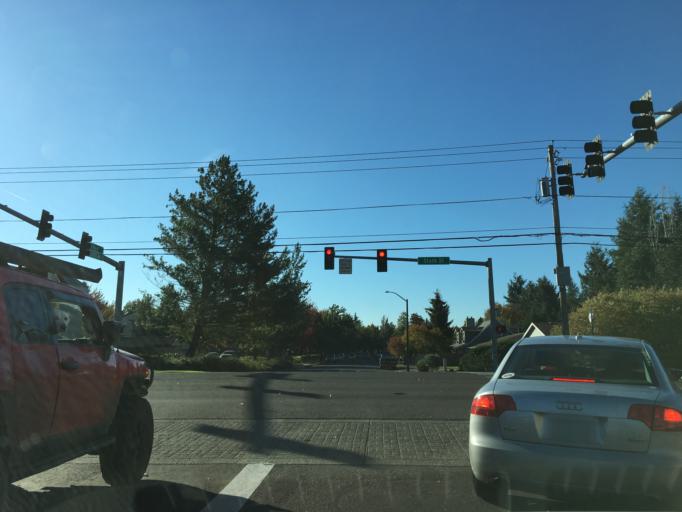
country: US
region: Oregon
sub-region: Multnomah County
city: Wood Village
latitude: 45.5193
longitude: -122.4011
